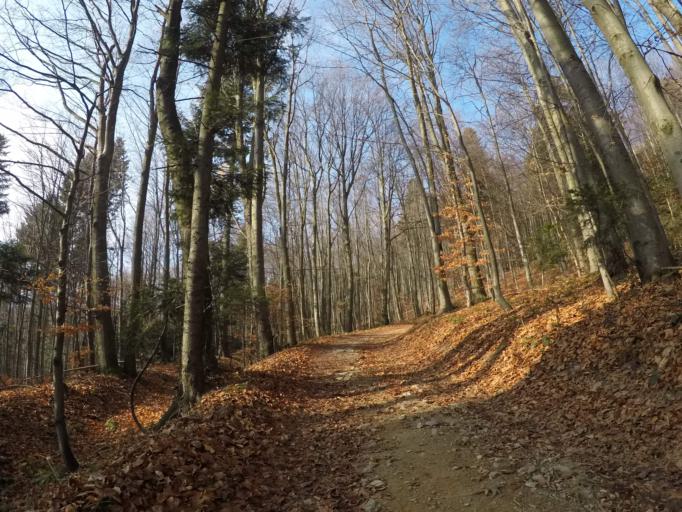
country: SK
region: Kosicky
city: Moldava nad Bodvou
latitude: 48.7634
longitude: 21.0782
